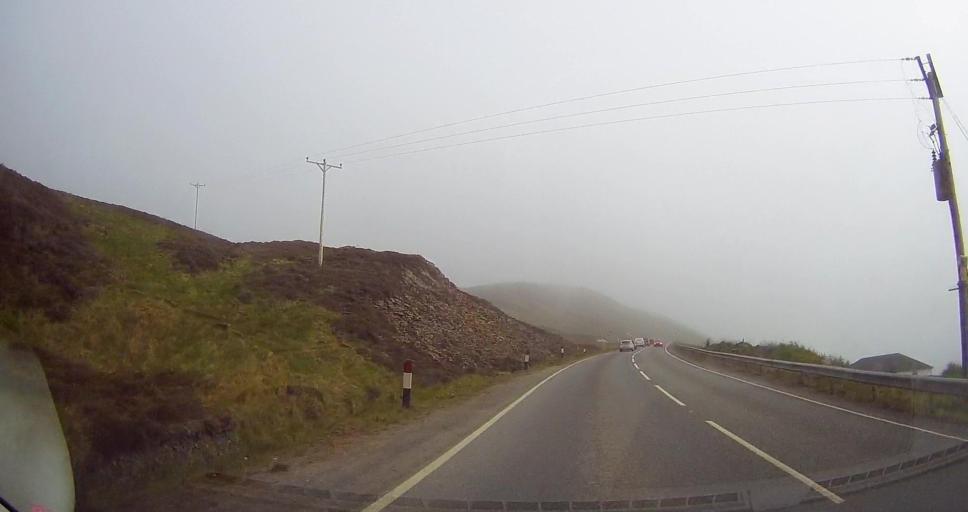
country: GB
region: Scotland
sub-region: Shetland Islands
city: Lerwick
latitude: 60.1418
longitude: -1.2613
